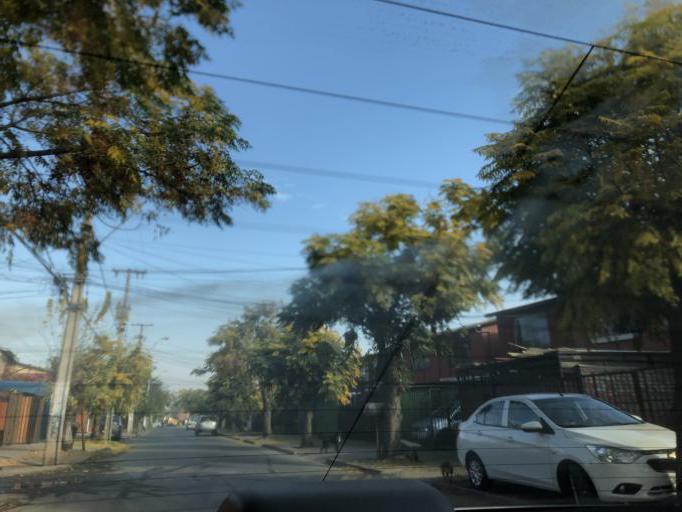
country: CL
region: Santiago Metropolitan
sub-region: Provincia de Cordillera
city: Puente Alto
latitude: -33.5898
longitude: -70.5651
